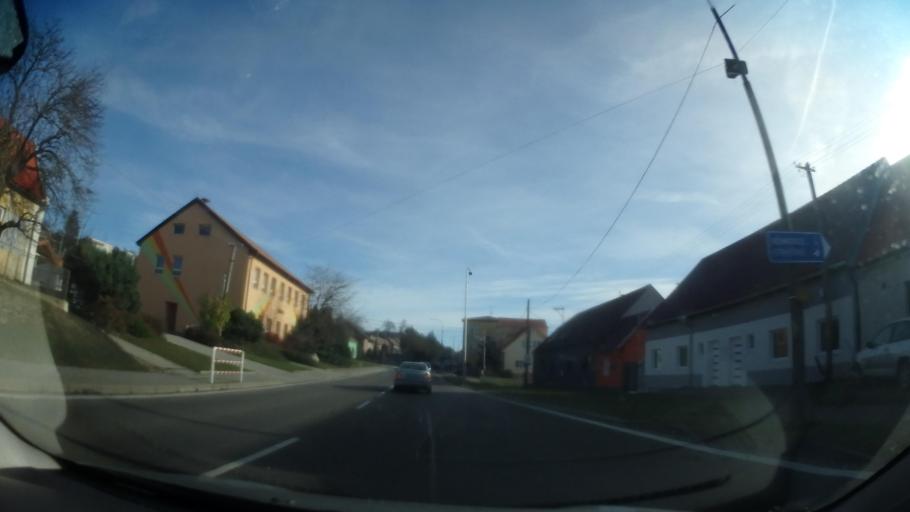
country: CZ
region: South Moravian
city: Sardice
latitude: 49.0100
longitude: 17.0437
